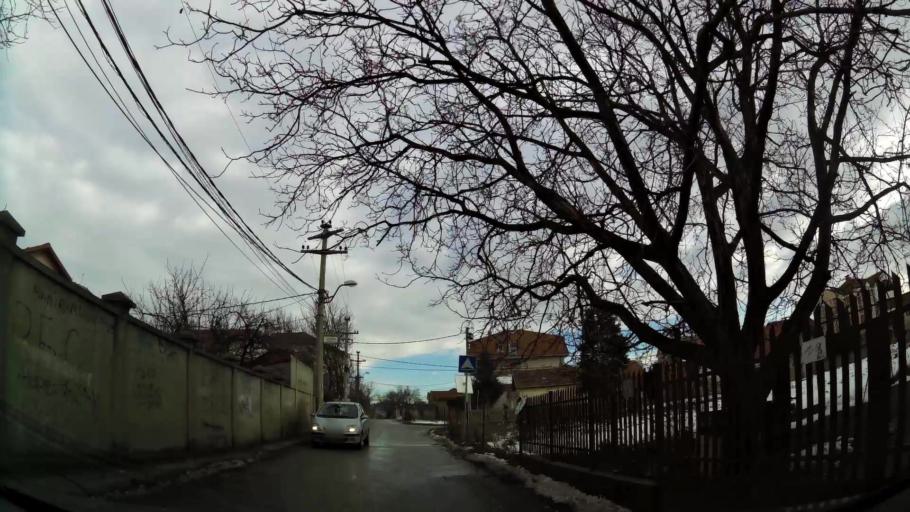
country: RS
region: Central Serbia
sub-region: Belgrade
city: Zemun
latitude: 44.8058
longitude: 20.3576
